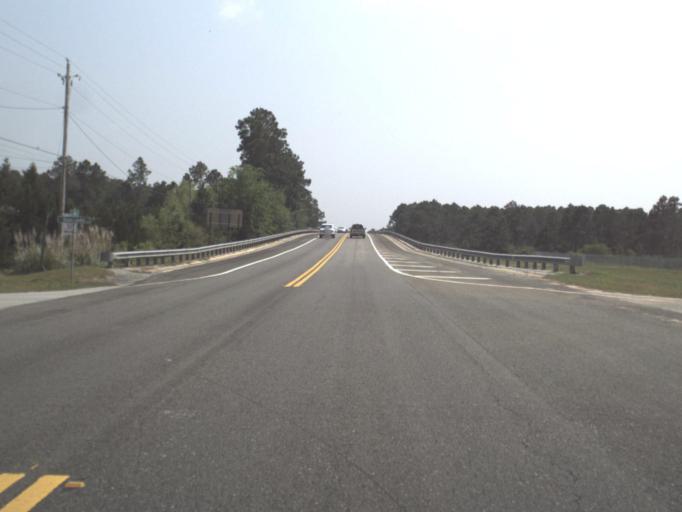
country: US
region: Florida
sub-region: Santa Rosa County
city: Bagdad
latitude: 30.5265
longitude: -87.0873
